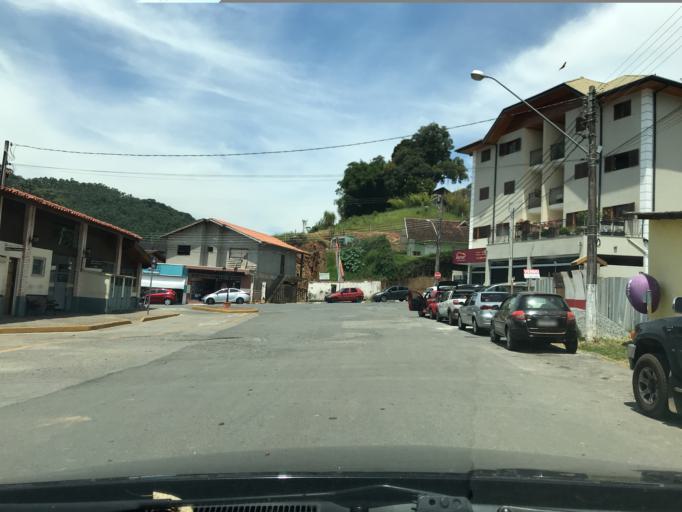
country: BR
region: Sao Paulo
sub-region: Campos Do Jordao
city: Campos do Jordao
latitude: -22.8258
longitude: -45.6666
